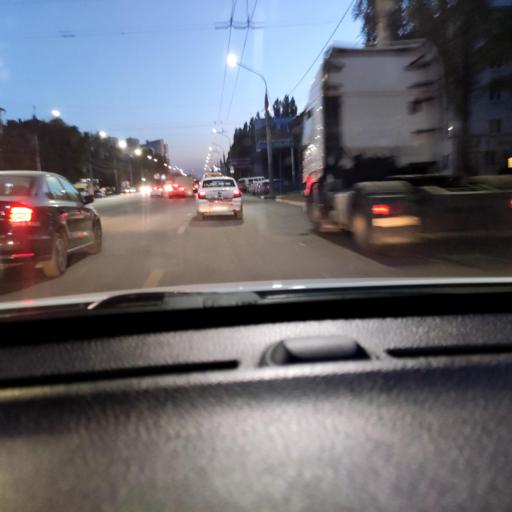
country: RU
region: Voronezj
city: Voronezh
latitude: 51.6684
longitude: 39.2504
